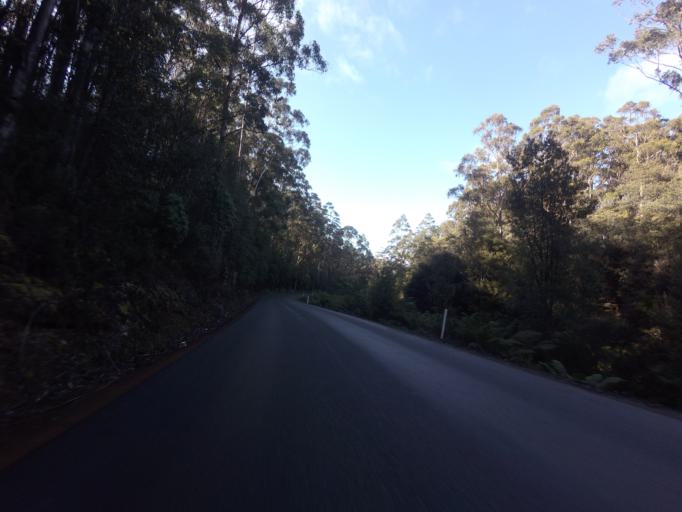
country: AU
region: Tasmania
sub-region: Huon Valley
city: Cygnet
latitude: -43.2610
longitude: 147.0077
